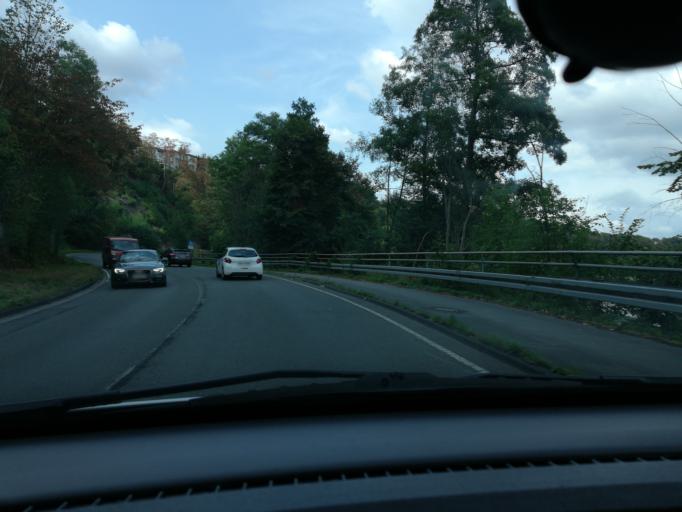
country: DE
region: North Rhine-Westphalia
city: Witten
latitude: 51.4287
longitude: 7.3015
